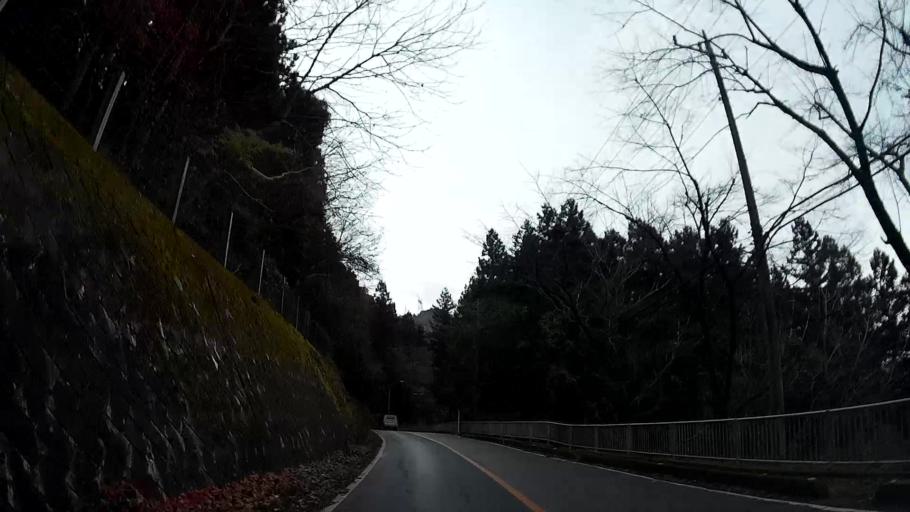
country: JP
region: Saitama
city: Chichibu
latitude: 35.9601
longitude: 139.0571
